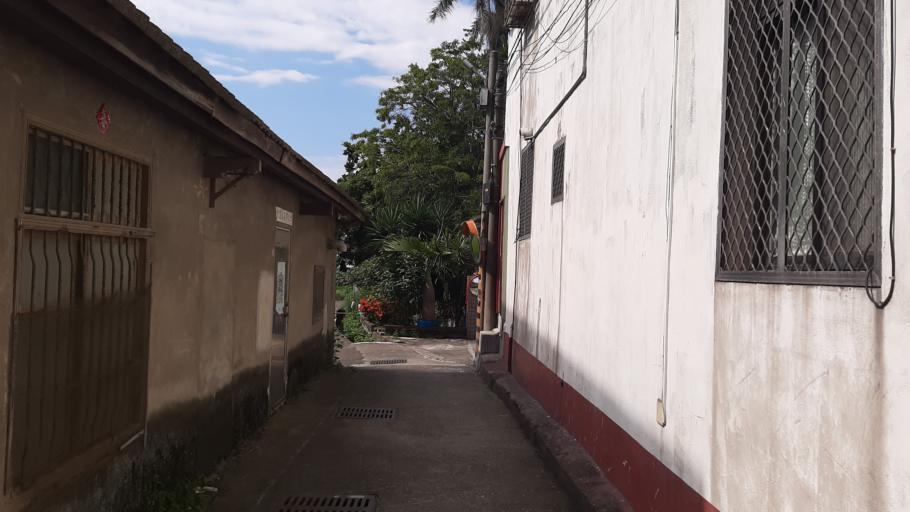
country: TW
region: Taiwan
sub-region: Changhua
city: Chang-hua
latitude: 24.2129
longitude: 120.5484
